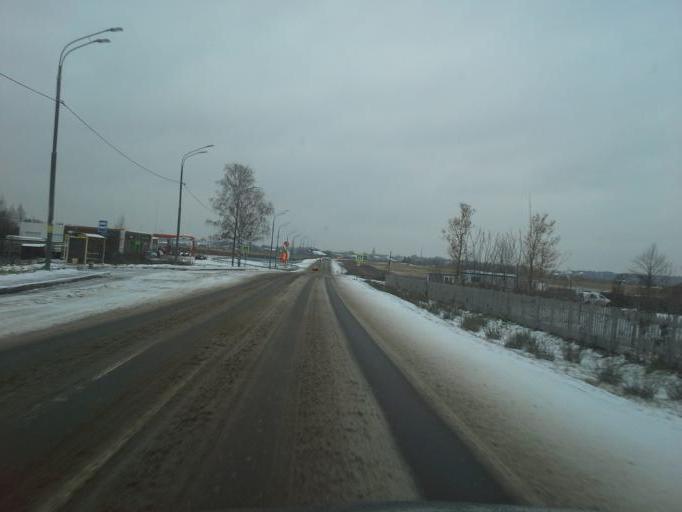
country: RU
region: Moskovskaya
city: Gorki Vtoryye
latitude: 55.7401
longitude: 37.1134
